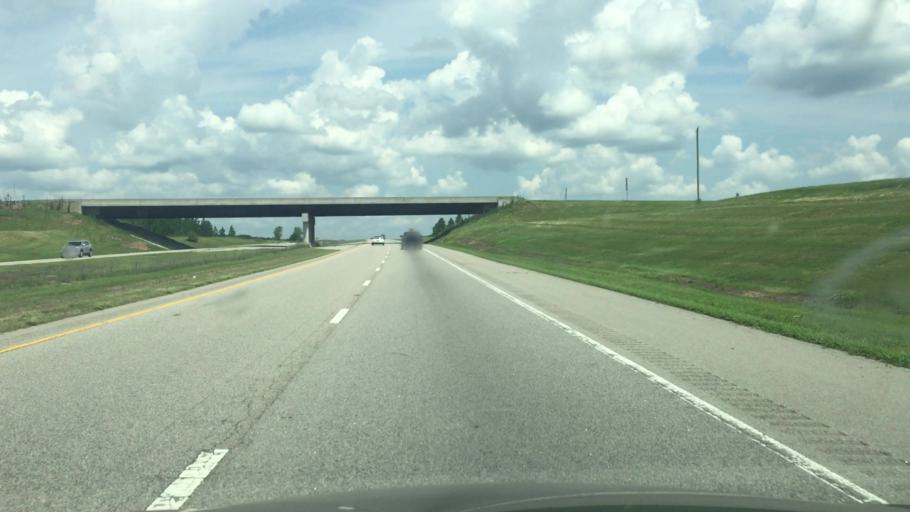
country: US
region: North Carolina
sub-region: Richmond County
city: Ellerbe
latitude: 35.1455
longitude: -79.7139
